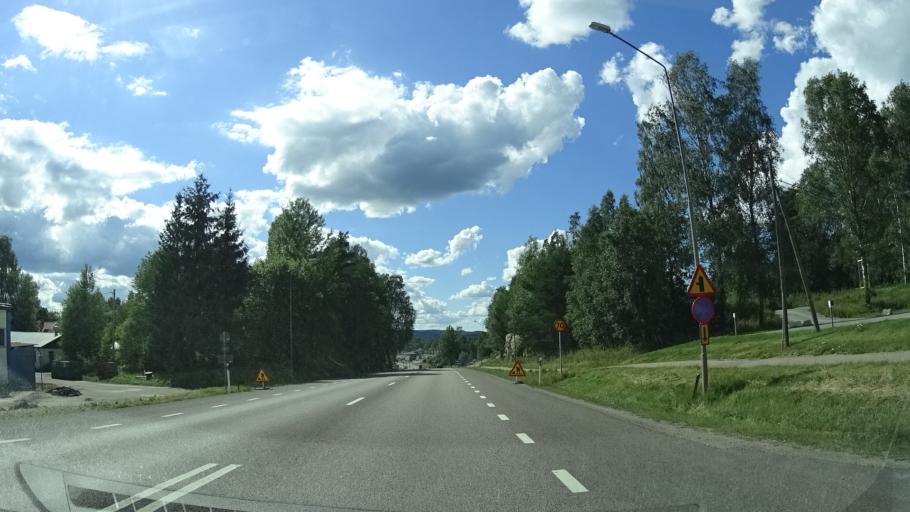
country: SE
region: Vaermland
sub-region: Arjangs Kommun
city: Toecksfors
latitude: 59.5073
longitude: 11.8526
